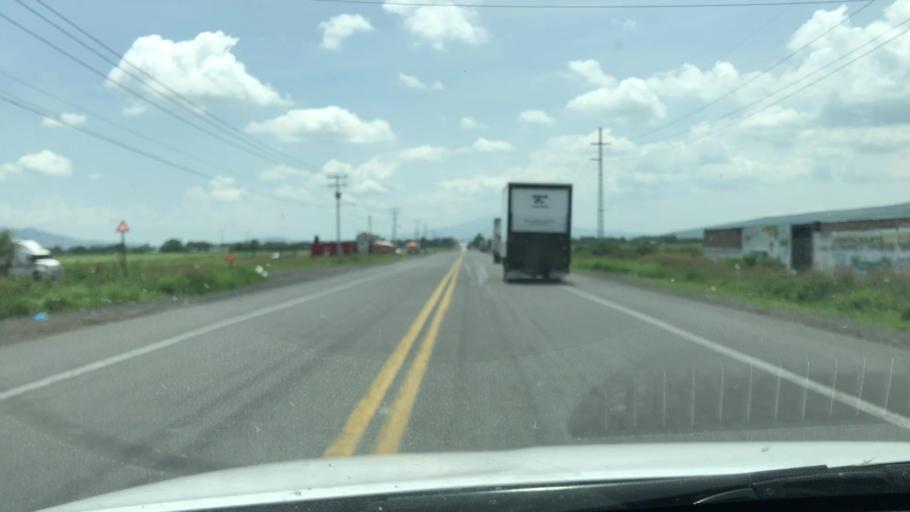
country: MX
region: Michoacan
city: Tanhuato de Guerrero
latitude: 20.2798
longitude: -102.3642
